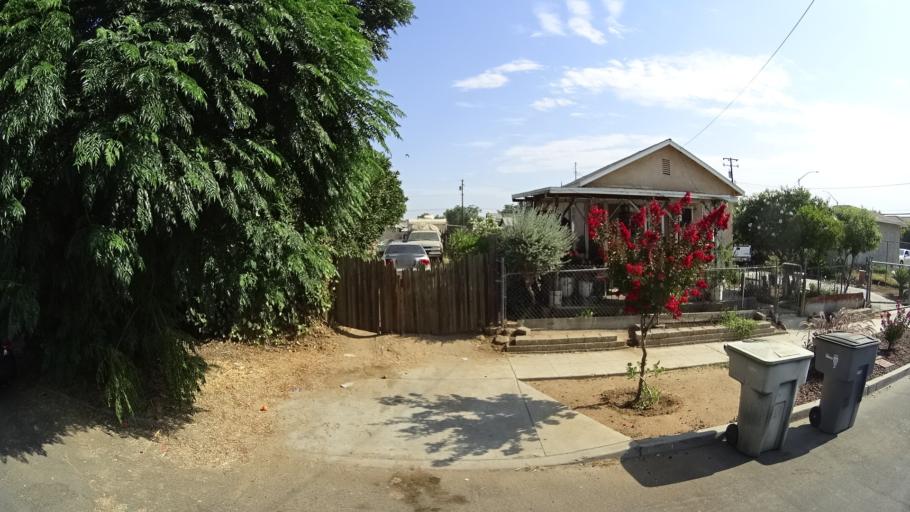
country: US
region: California
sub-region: Fresno County
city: West Park
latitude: 36.7196
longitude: -119.8116
